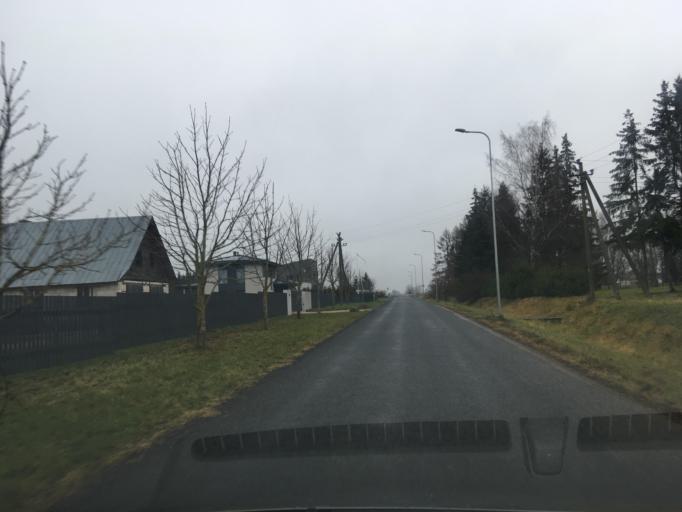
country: EE
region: Tartu
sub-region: Tartu linn
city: Tartu
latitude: 58.3542
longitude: 26.8710
